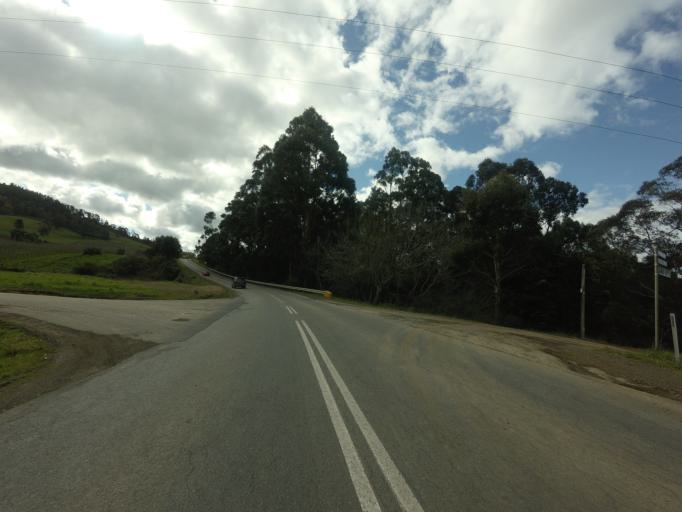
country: AU
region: Tasmania
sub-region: Huon Valley
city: Geeveston
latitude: -43.1899
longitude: 146.9597
